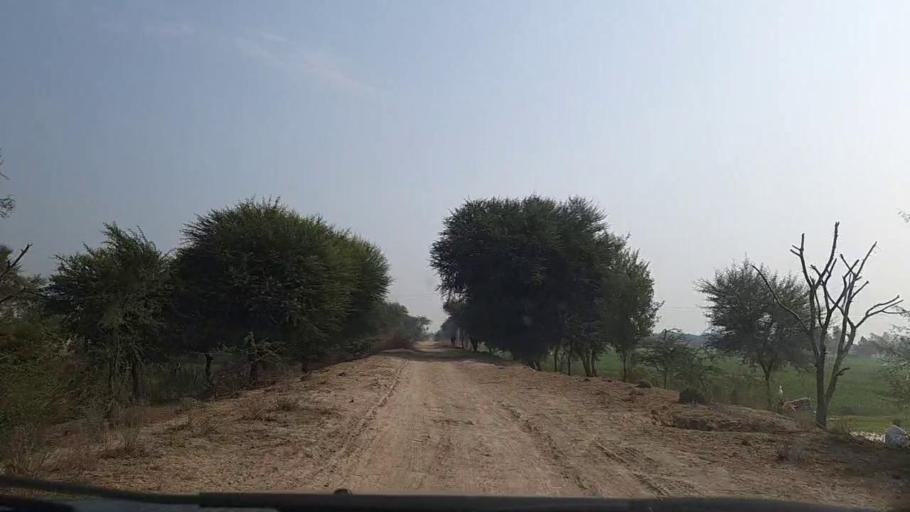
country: PK
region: Sindh
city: Sanghar
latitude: 26.0508
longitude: 68.9814
